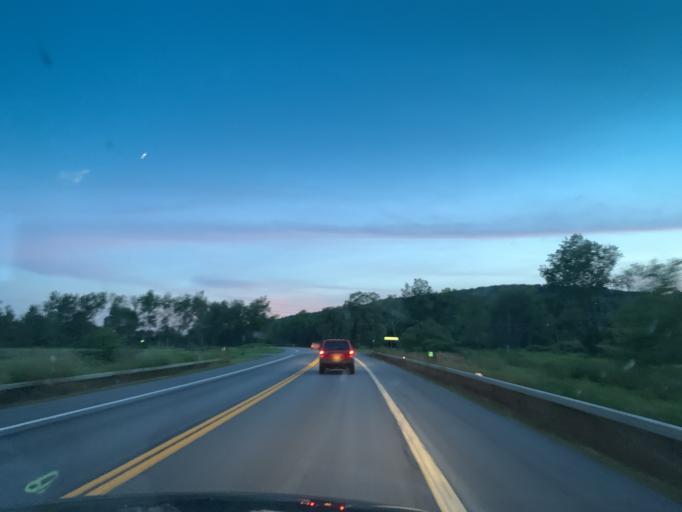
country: US
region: New York
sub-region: Chenango County
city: New Berlin
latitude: 42.5629
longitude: -75.3564
